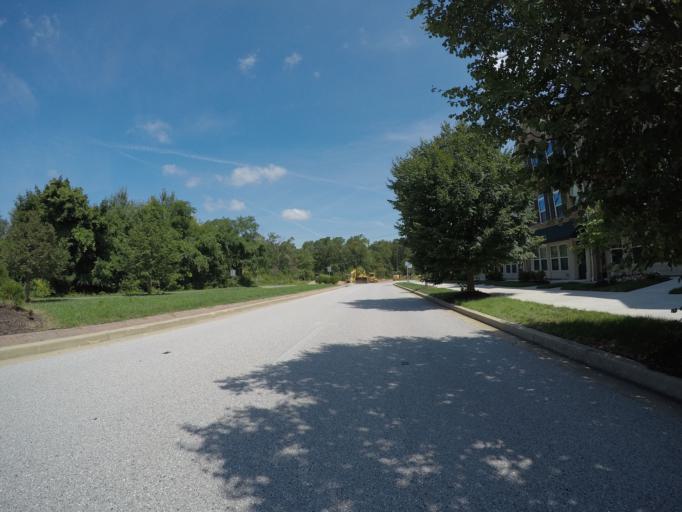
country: US
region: Maryland
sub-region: Anne Arundel County
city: Odenton
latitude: 39.0908
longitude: -76.7073
